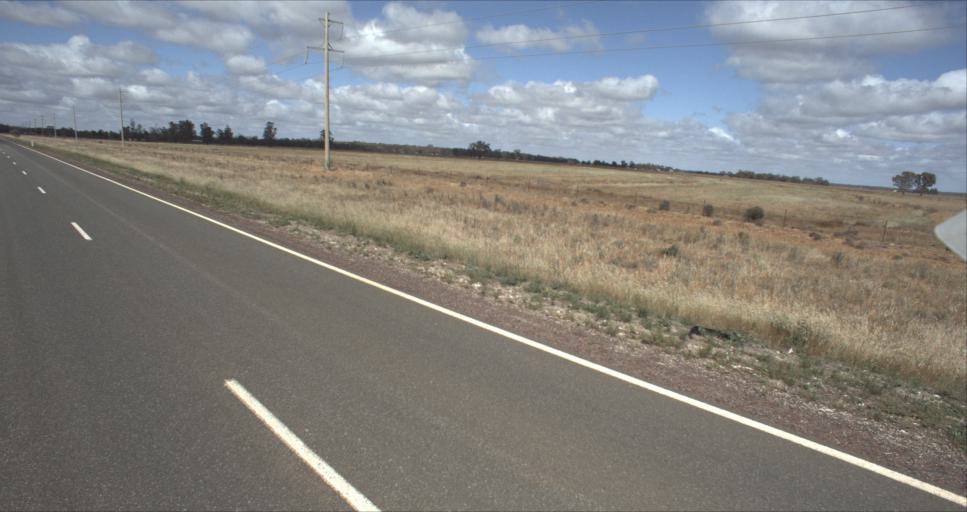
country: AU
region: New South Wales
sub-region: Murrumbidgee Shire
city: Darlington Point
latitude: -34.5864
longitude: 146.1642
